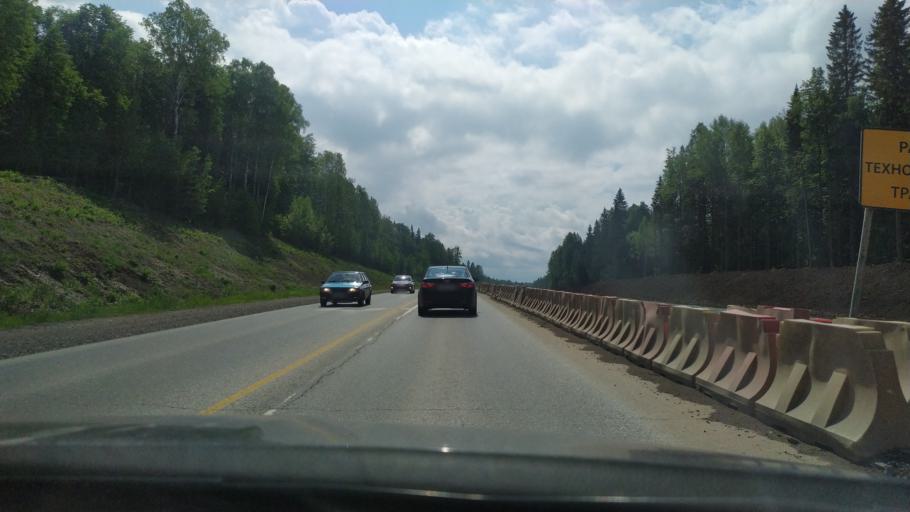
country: RU
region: Perm
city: Novyye Lyady
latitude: 58.0824
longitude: 56.4305
